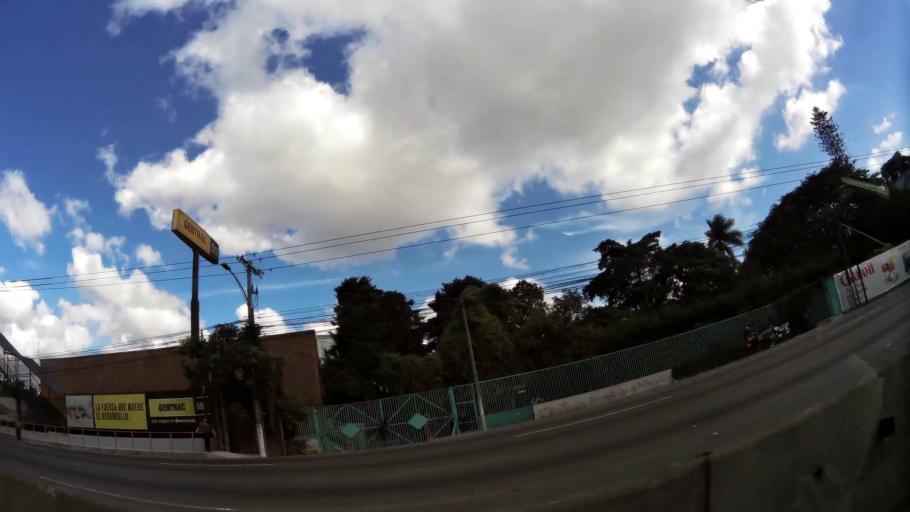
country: GT
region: Guatemala
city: Villa Nueva
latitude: 14.5673
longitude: -90.5742
